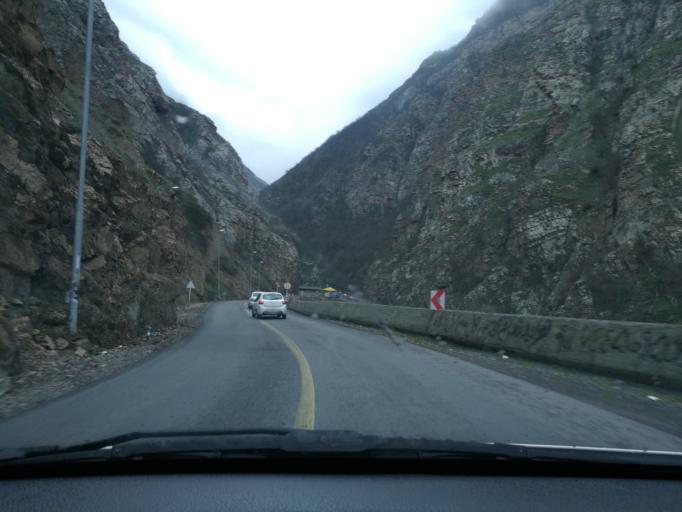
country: IR
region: Mazandaran
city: Chalus
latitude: 36.2638
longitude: 51.2638
